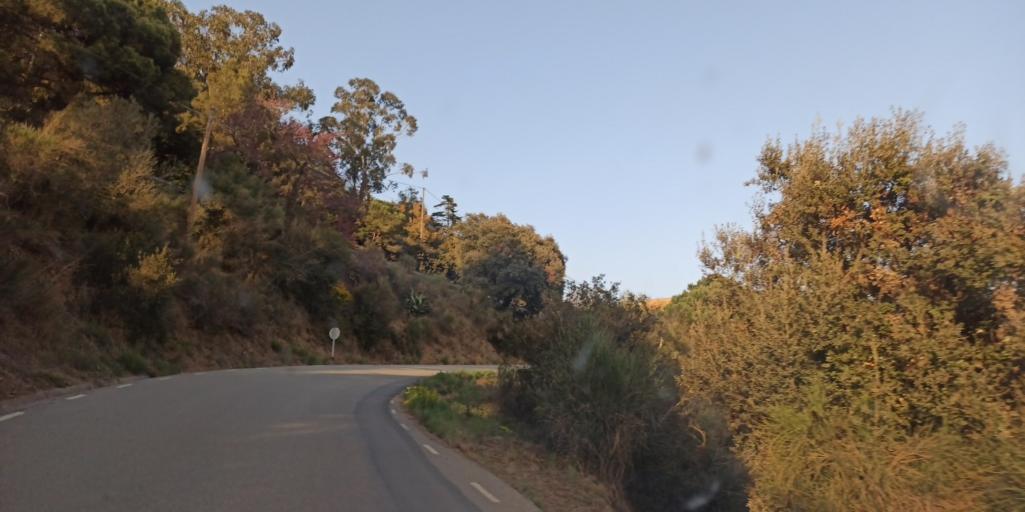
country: ES
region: Catalonia
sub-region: Provincia de Barcelona
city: Sant Just Desvern
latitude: 41.4079
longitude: 2.0877
